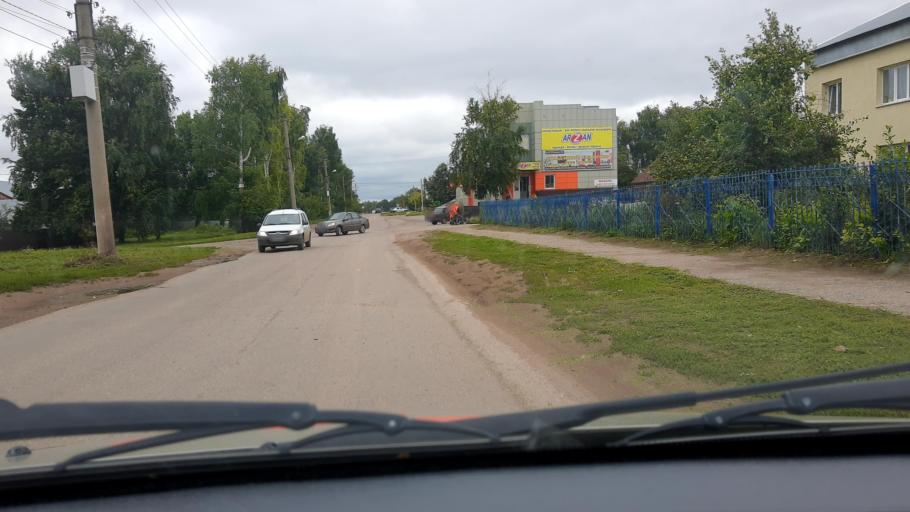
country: RU
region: Bashkortostan
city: Chishmy
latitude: 54.5912
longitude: 55.3766
